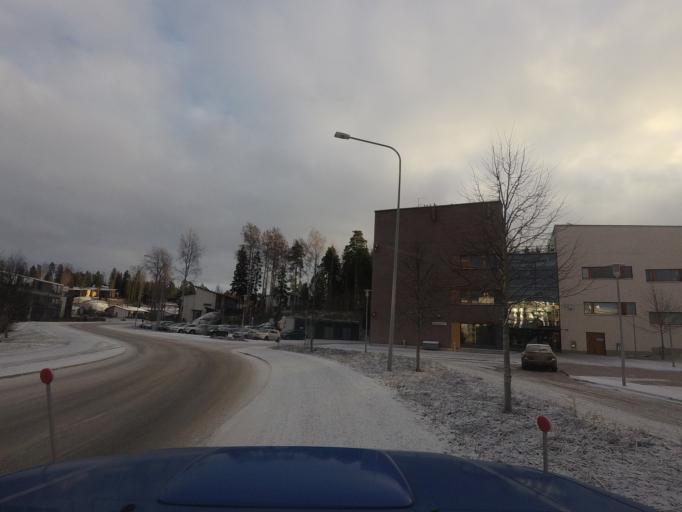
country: FI
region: Uusimaa
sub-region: Helsinki
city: Kauniainen
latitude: 60.2054
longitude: 24.7110
